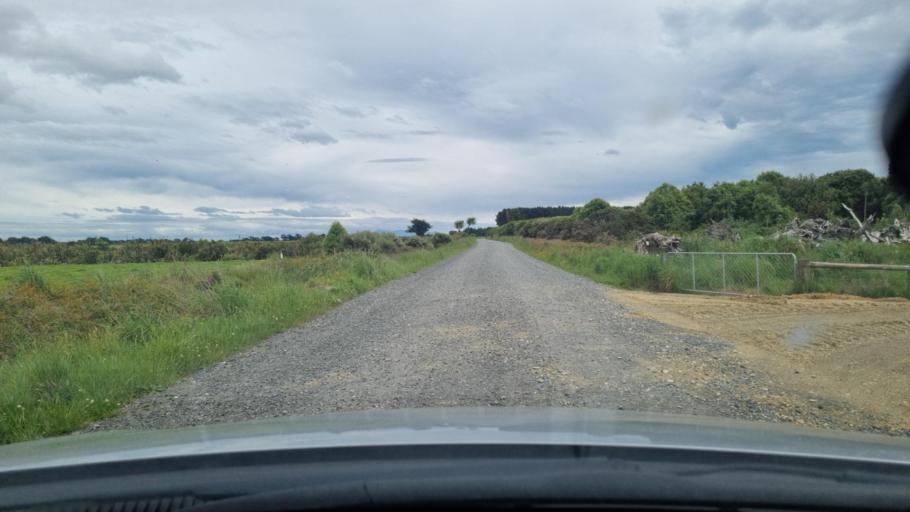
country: NZ
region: Southland
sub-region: Invercargill City
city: Invercargill
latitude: -46.4039
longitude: 168.2794
